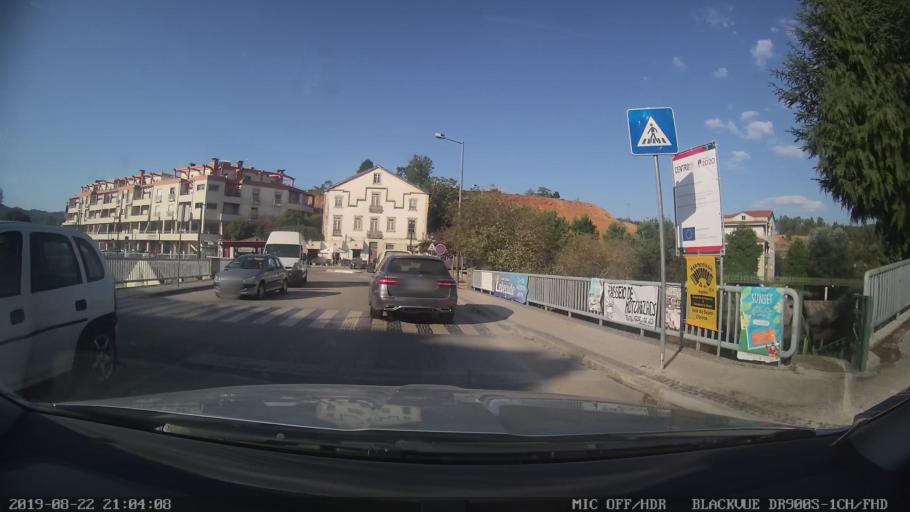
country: PT
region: Castelo Branco
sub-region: Serta
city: Serta
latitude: 39.8054
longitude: -8.1001
